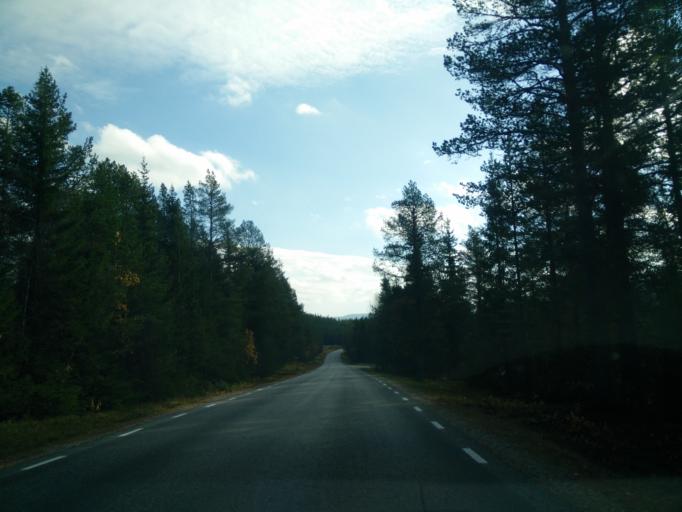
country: SE
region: Jaemtland
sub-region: Are Kommun
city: Are
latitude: 62.5556
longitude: 12.5699
